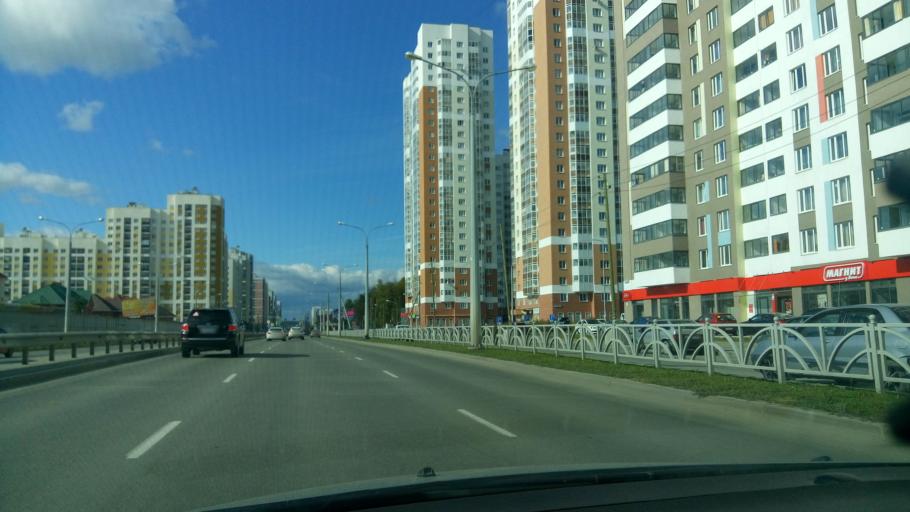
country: RU
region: Sverdlovsk
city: Sovkhoznyy
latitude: 56.7865
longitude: 60.5336
